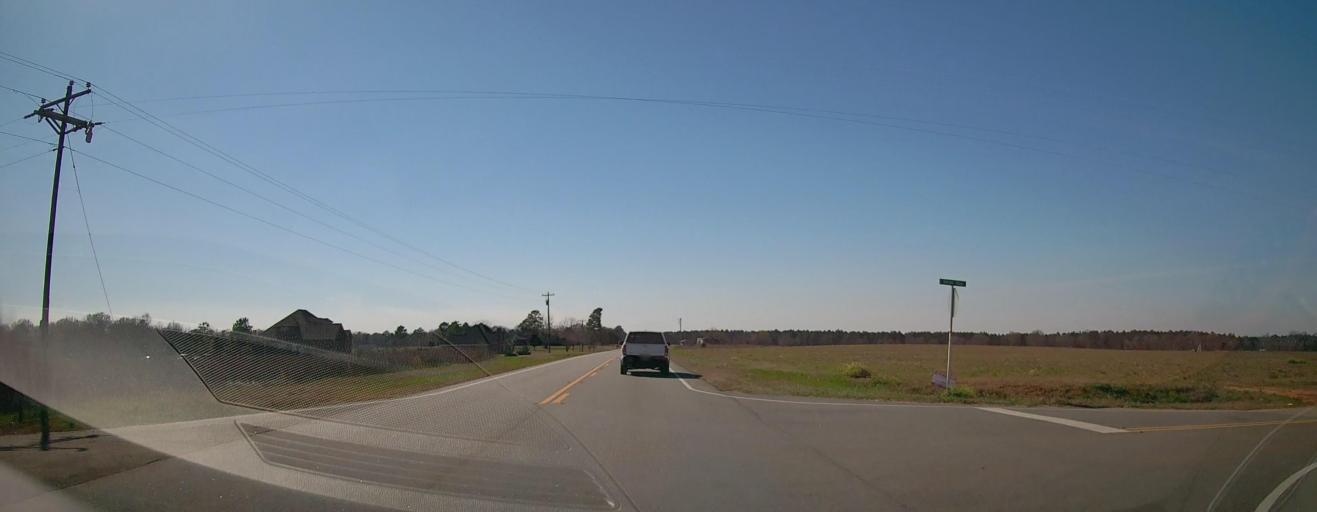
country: US
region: Georgia
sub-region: Dooly County
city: Unadilla
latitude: 32.3379
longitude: -83.8370
